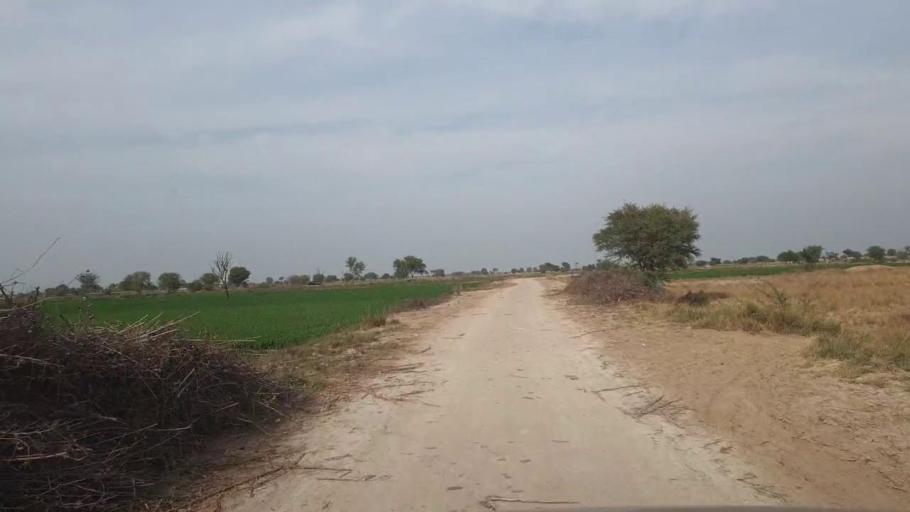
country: PK
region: Sindh
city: Shahpur Chakar
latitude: 26.1119
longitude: 68.5048
